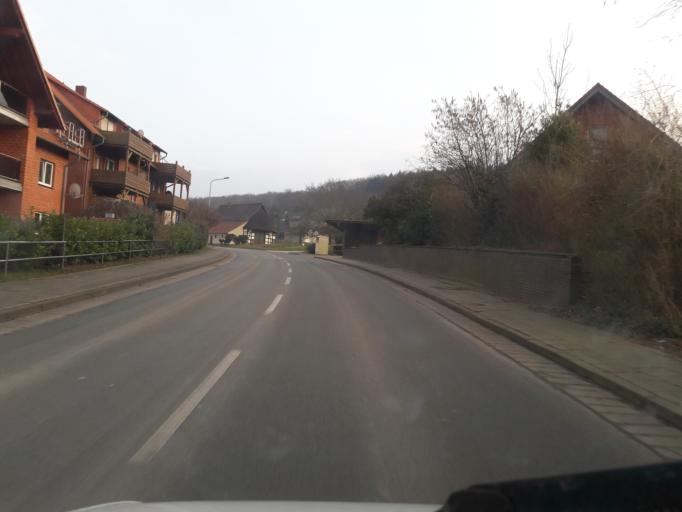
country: DE
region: North Rhine-Westphalia
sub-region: Regierungsbezirk Detmold
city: Hille
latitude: 52.2917
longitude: 8.7270
